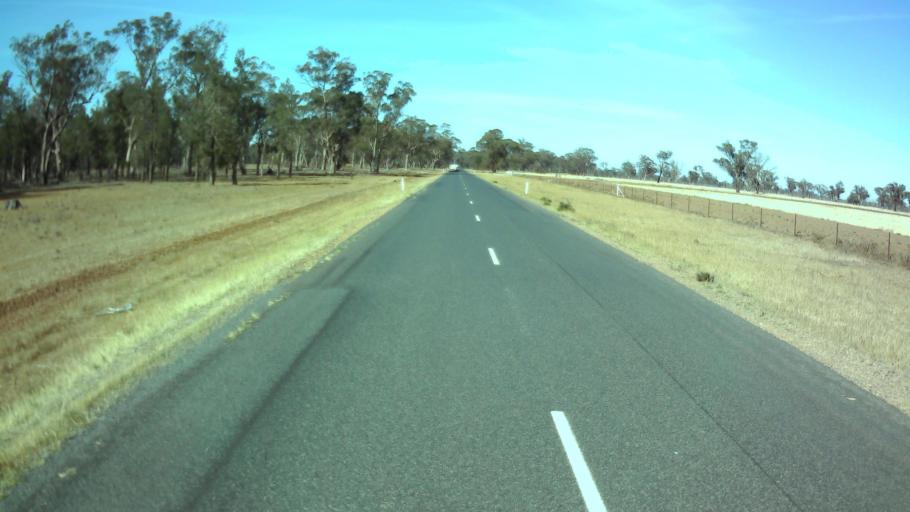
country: AU
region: New South Wales
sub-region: Weddin
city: Grenfell
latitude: -34.1300
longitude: 147.7967
